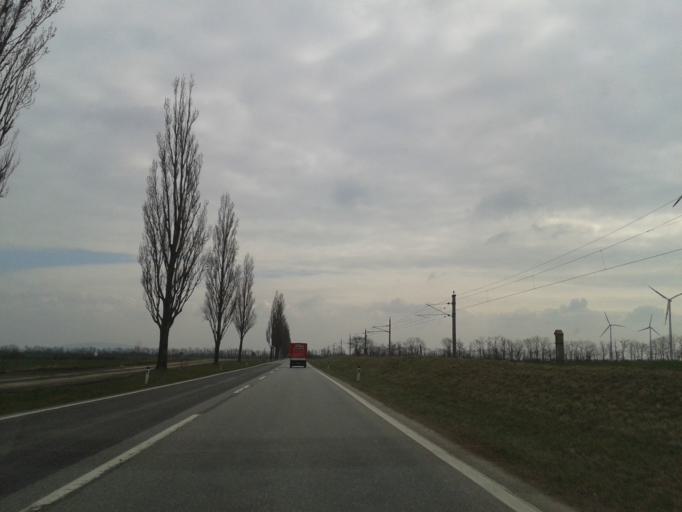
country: AT
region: Lower Austria
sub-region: Politischer Bezirk Bruck an der Leitha
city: Scharndorf
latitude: 48.1082
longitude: 16.7415
